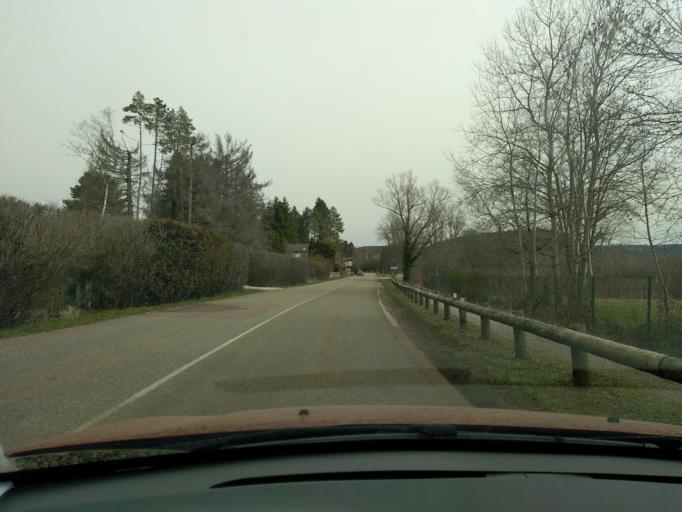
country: FR
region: Franche-Comte
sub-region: Departement du Jura
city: Clairvaux-les-Lacs
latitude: 46.6765
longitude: 5.7749
